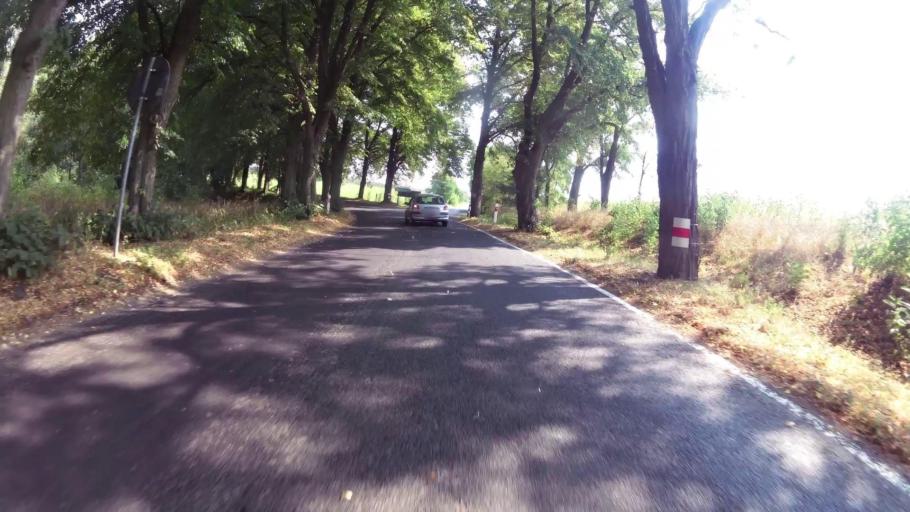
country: PL
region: West Pomeranian Voivodeship
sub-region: Powiat gryfinski
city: Moryn
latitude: 52.8222
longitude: 14.4308
